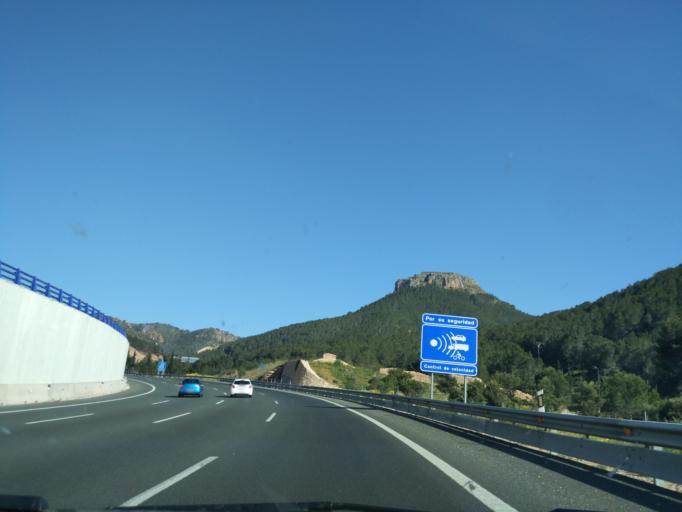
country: ES
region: Murcia
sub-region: Murcia
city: Alcantarilla
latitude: 37.9091
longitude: -1.1625
